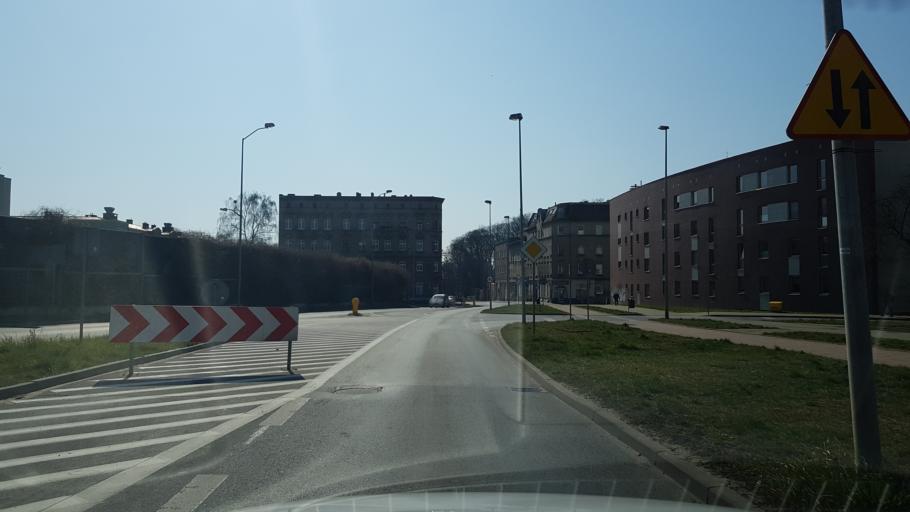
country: PL
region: West Pomeranian Voivodeship
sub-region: Szczecin
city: Szczecin
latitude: 53.4535
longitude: 14.5439
